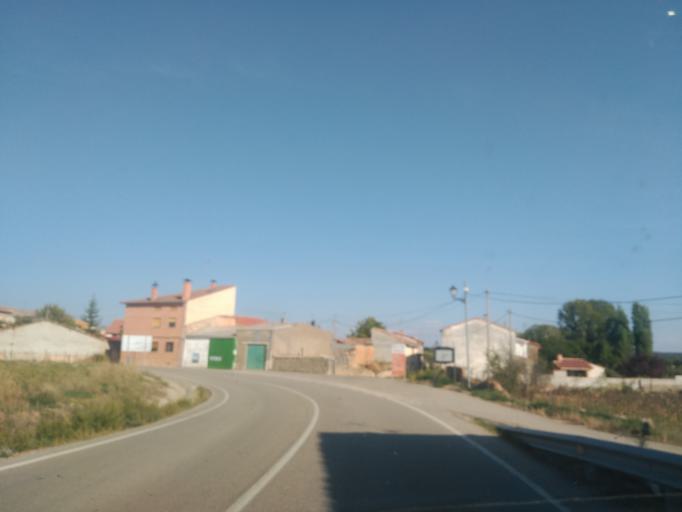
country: ES
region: Castille and Leon
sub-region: Provincia de Burgos
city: Brazacorta
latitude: 41.7192
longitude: -3.3451
